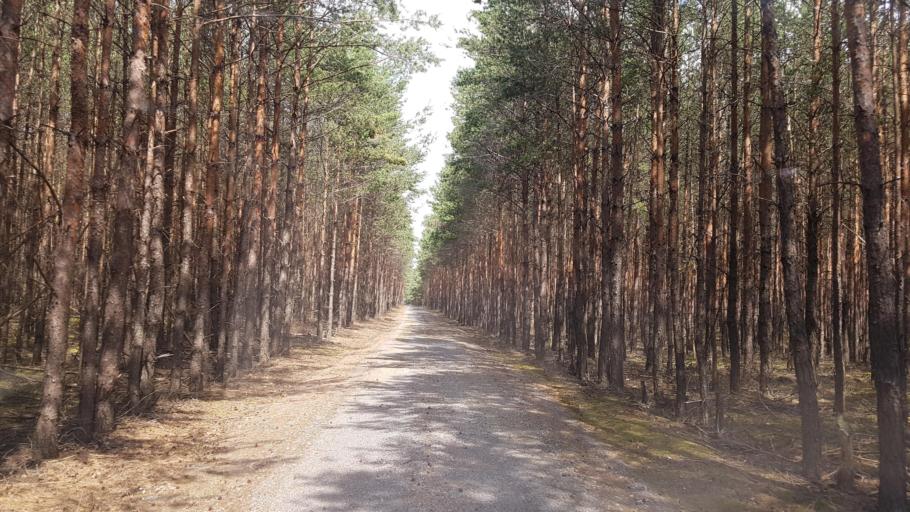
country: DE
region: Brandenburg
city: Crinitz
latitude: 51.7025
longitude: 13.8202
